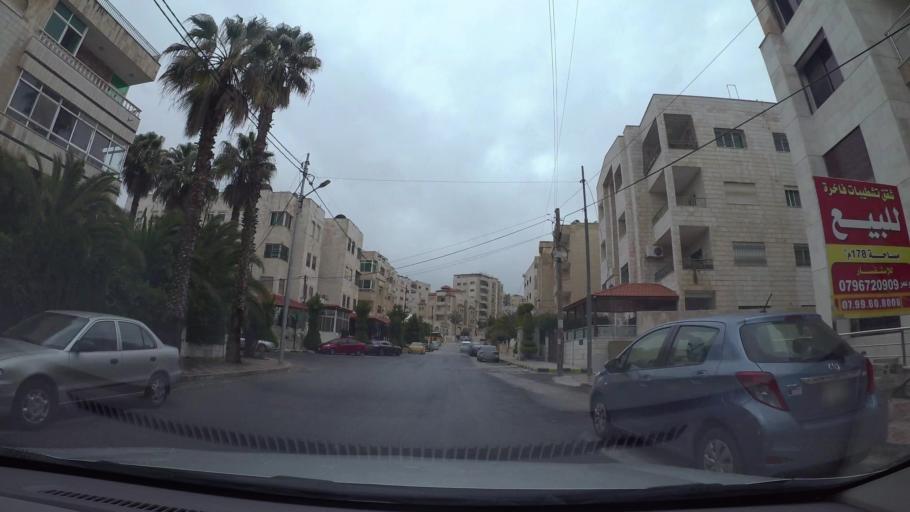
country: JO
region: Amman
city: Al Jubayhah
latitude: 31.9869
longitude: 35.8598
